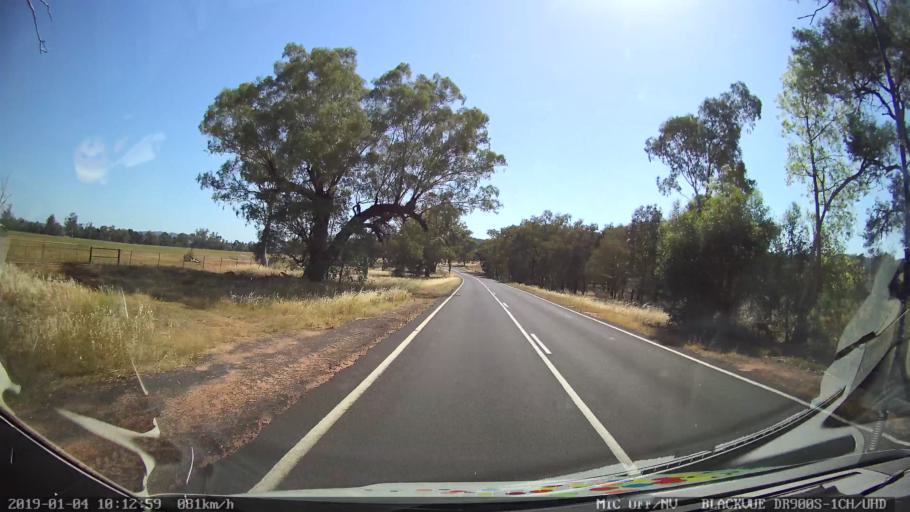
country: AU
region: New South Wales
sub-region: Cabonne
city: Canowindra
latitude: -33.4102
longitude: 148.4019
